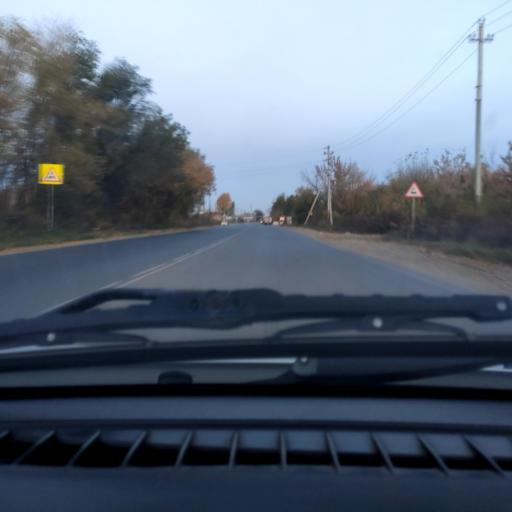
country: RU
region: Samara
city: Tol'yatti
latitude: 53.5294
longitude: 49.4703
